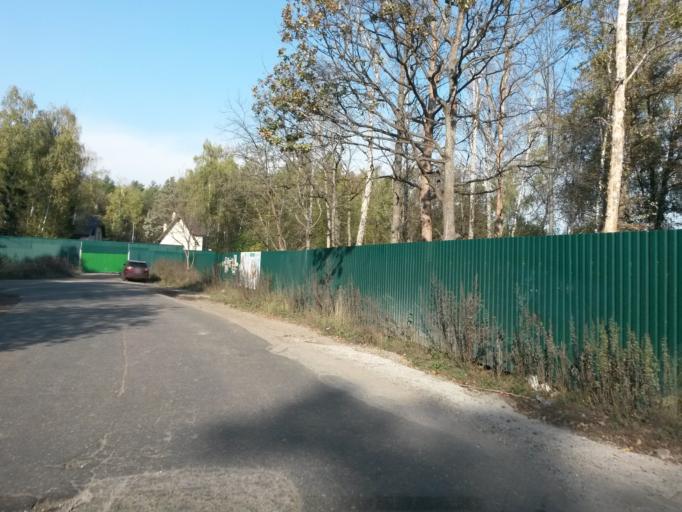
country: RU
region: Moskovskaya
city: Lyubuchany
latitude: 55.3019
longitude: 37.6239
